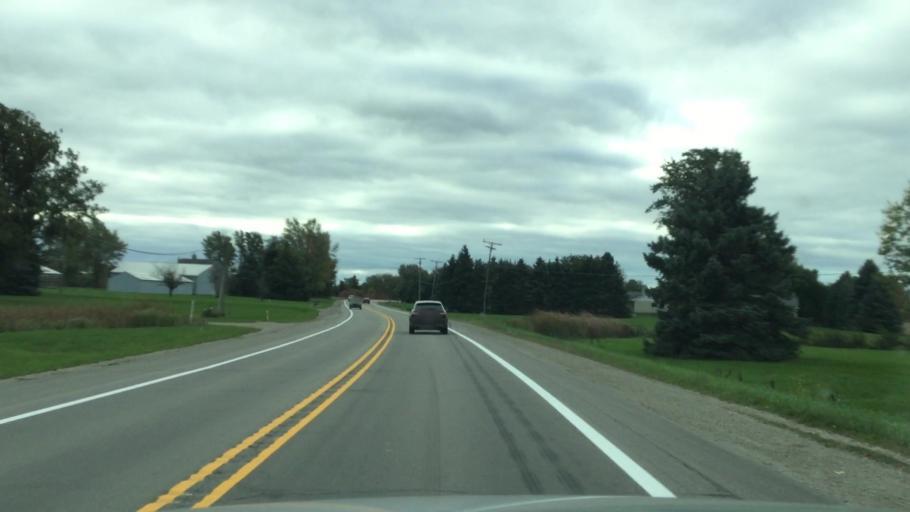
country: US
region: Michigan
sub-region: Macomb County
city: Memphis
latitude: 42.8581
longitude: -82.7661
